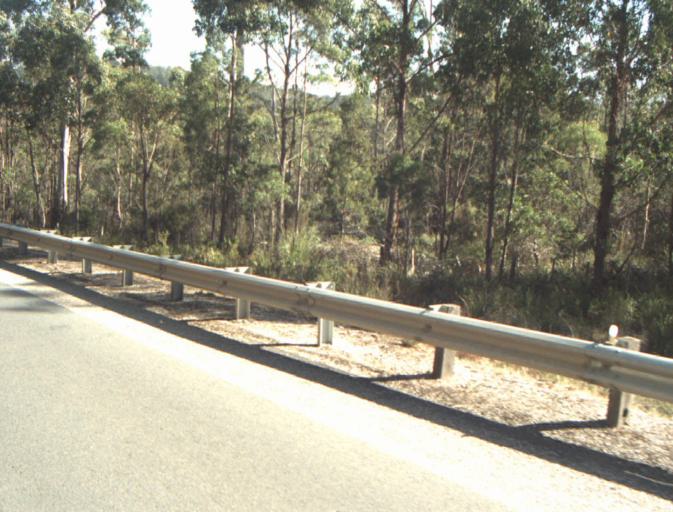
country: AU
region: Tasmania
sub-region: Launceston
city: Mayfield
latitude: -41.3209
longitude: 147.1883
